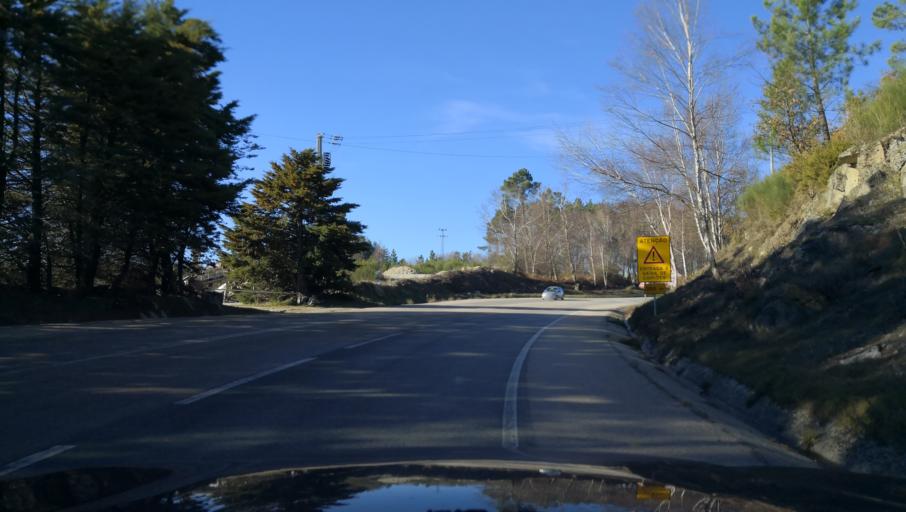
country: PT
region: Vila Real
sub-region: Vila Pouca de Aguiar
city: Vila Pouca de Aguiar
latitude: 41.4906
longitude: -7.6684
